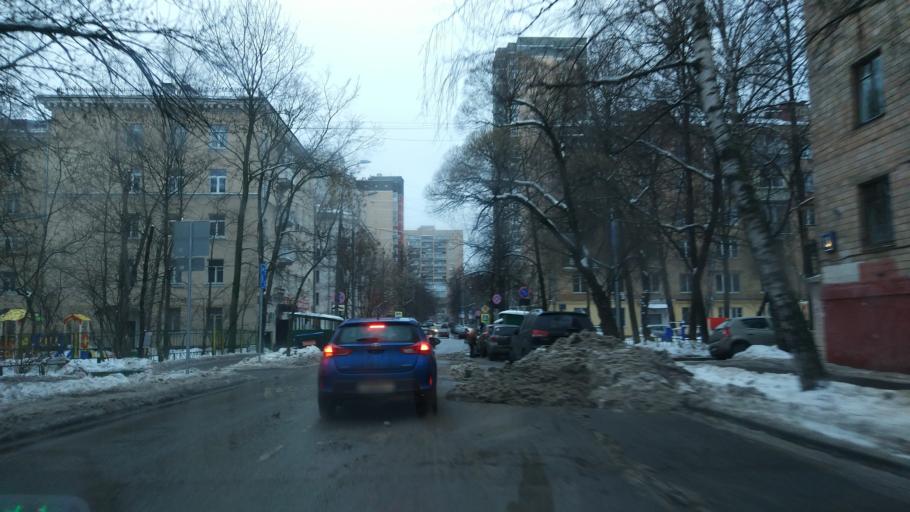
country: RU
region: Moskovskaya
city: Izmaylovo
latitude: 55.7911
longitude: 37.7957
